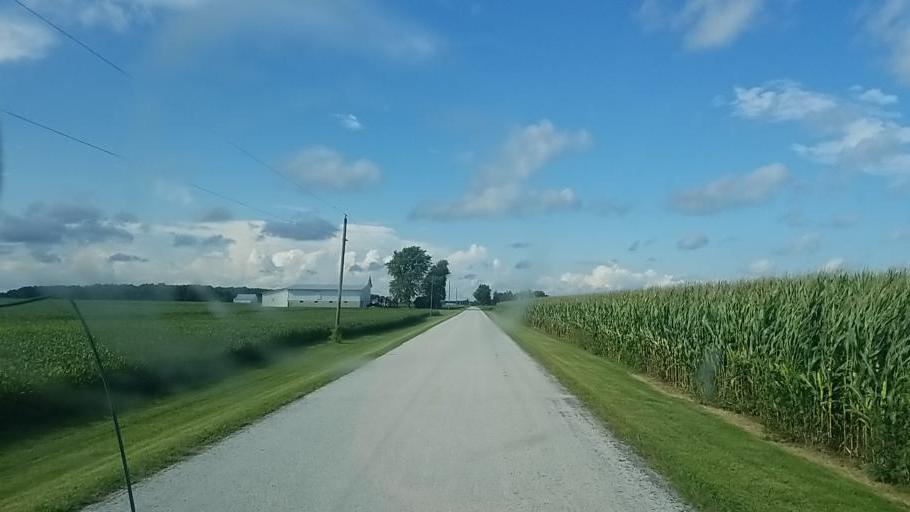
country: US
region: Ohio
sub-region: Hardin County
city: Forest
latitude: 40.7378
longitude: -83.5159
